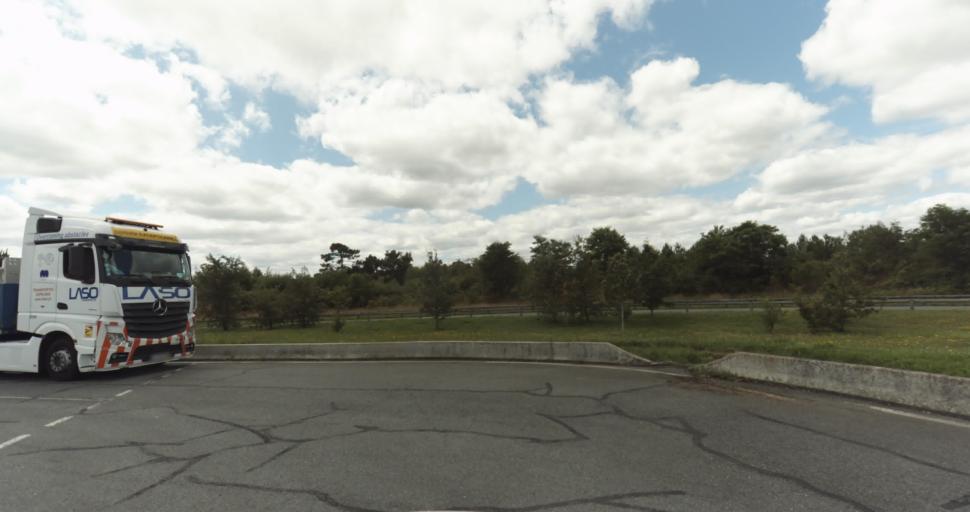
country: FR
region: Aquitaine
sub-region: Departement de la Gironde
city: Bazas
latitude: 44.4455
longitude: -0.2450
